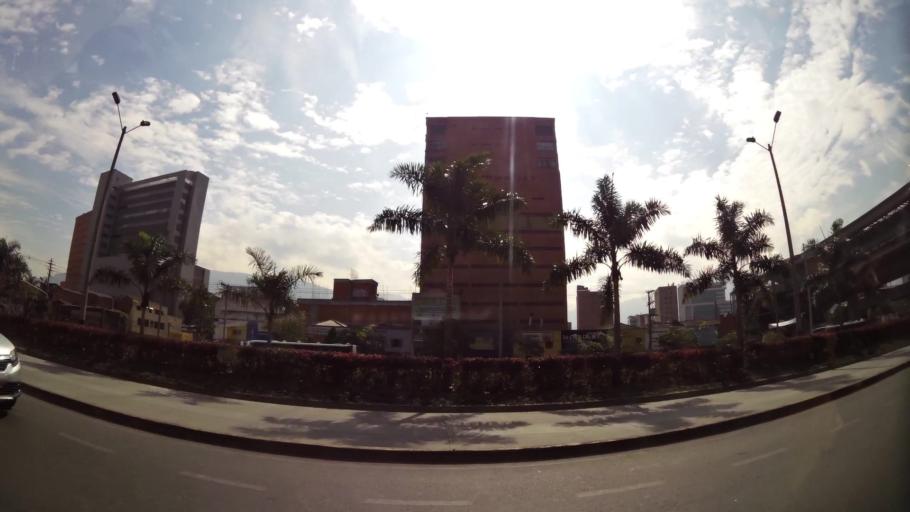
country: CO
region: Antioquia
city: Medellin
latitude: 6.2497
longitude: -75.5752
